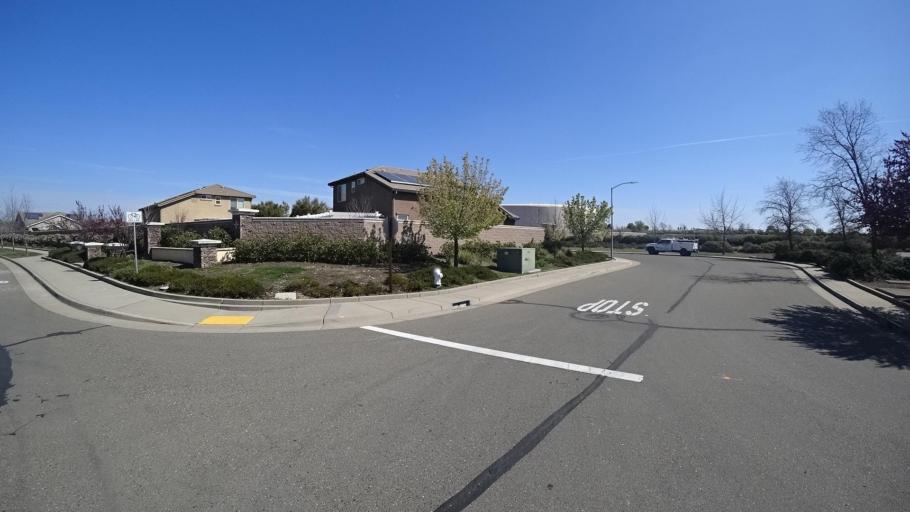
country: US
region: California
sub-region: Sacramento County
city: Rancho Cordova
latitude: 38.5756
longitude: -121.2672
